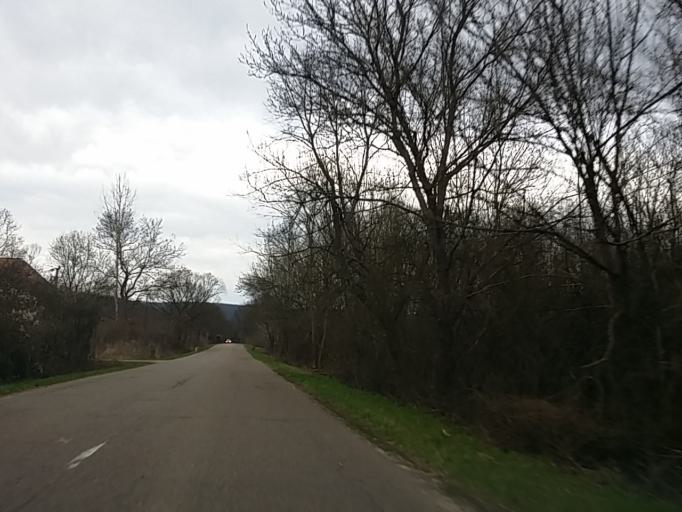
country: HU
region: Heves
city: Sirok
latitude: 47.9081
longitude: 20.1782
